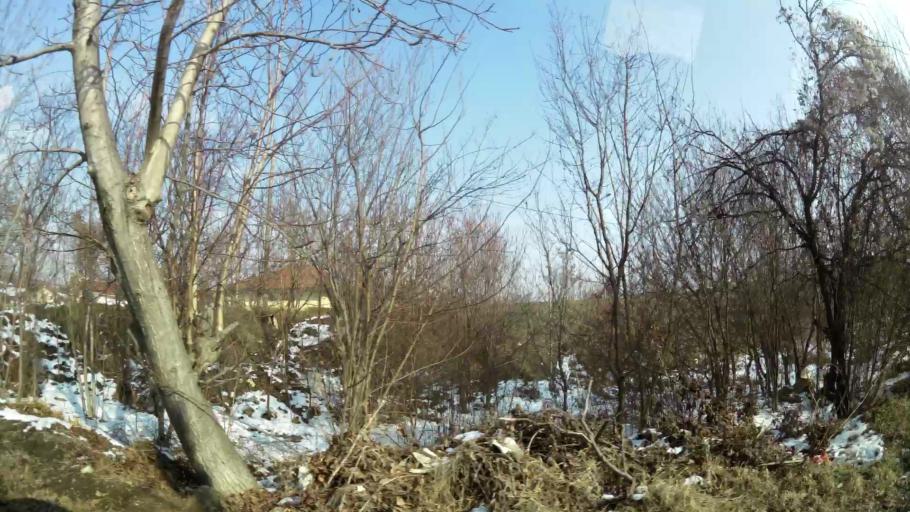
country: MK
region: Suto Orizari
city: Suto Orizare
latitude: 42.0249
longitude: 21.3835
